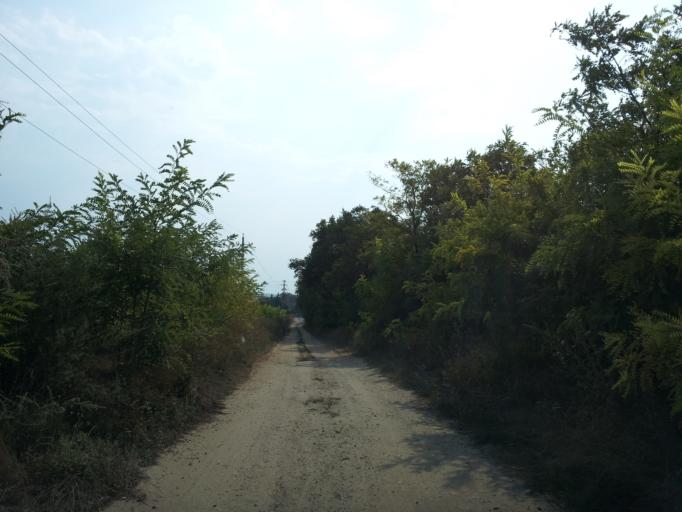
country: HU
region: Gyor-Moson-Sopron
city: Gyor
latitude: 47.6517
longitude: 17.6747
